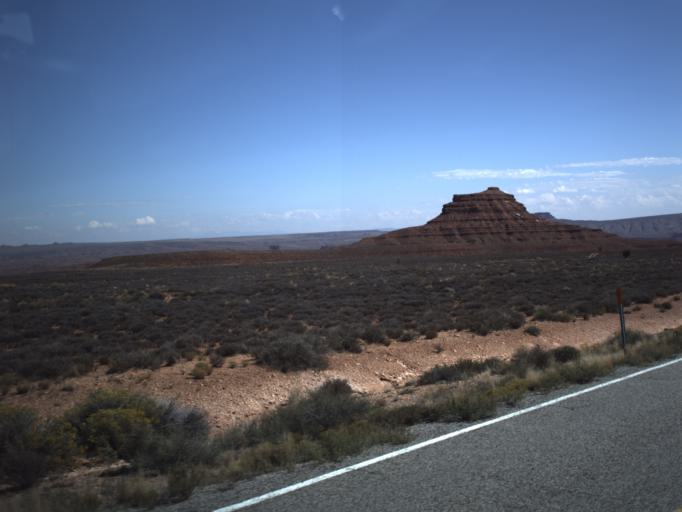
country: US
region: Utah
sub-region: San Juan County
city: Blanding
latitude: 37.2446
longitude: -109.9150
